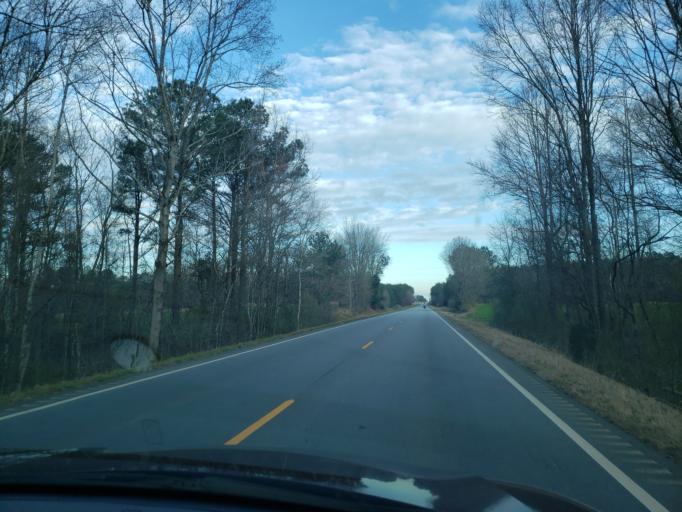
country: US
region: Alabama
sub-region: Randolph County
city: Wedowee
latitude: 33.2656
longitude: -85.4578
